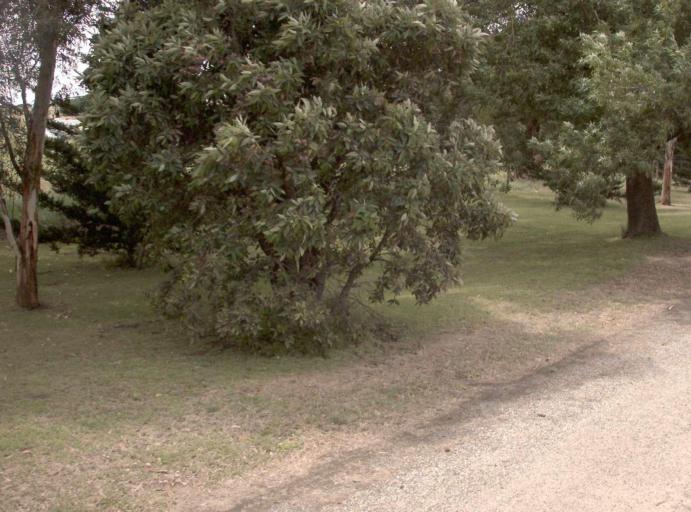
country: AU
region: Victoria
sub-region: Wellington
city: Sale
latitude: -37.9772
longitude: 146.9877
